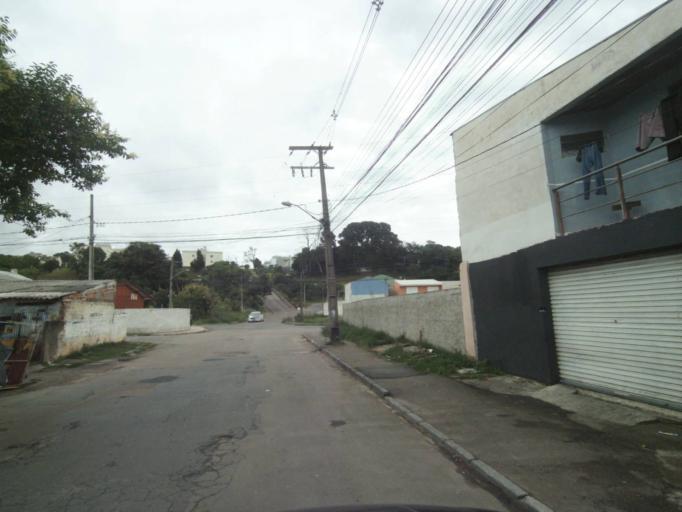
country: BR
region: Parana
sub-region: Curitiba
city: Curitiba
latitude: -25.4696
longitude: -49.3232
